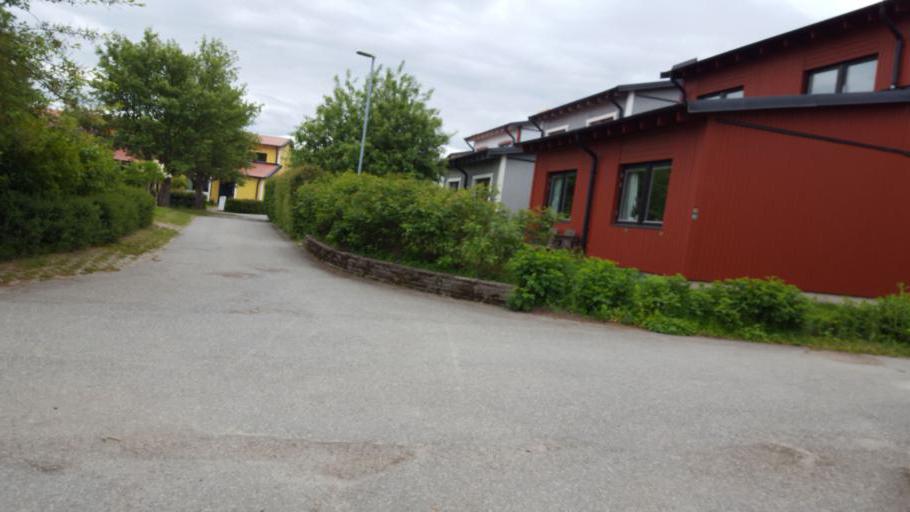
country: SE
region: Stockholm
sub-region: Upplands Vasby Kommun
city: Upplands Vaesby
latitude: 59.5092
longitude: 17.8879
